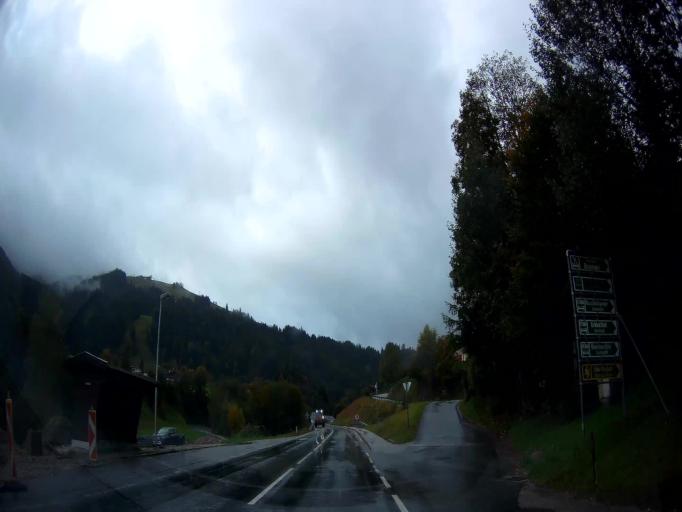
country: AT
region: Salzburg
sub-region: Politischer Bezirk Zell am See
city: Leogang
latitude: 47.4404
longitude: 12.7270
